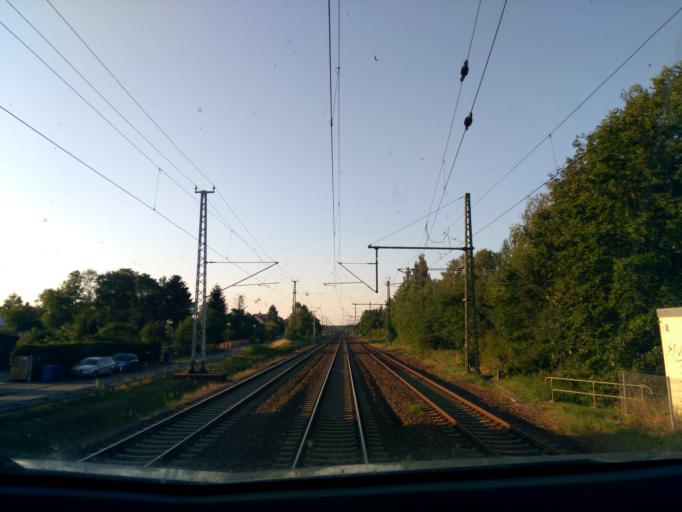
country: DE
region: Brandenburg
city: Halbe
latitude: 52.1144
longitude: 13.6954
